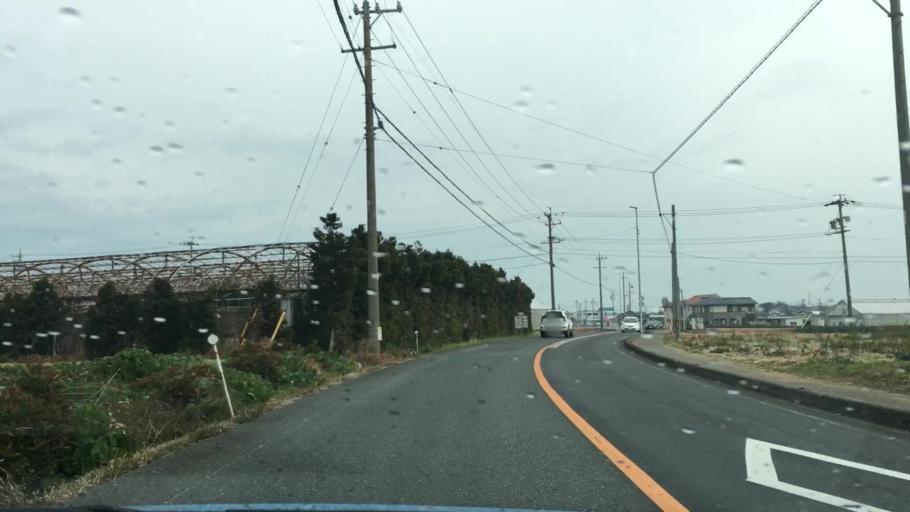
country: JP
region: Aichi
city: Tahara
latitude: 34.6958
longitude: 137.2693
